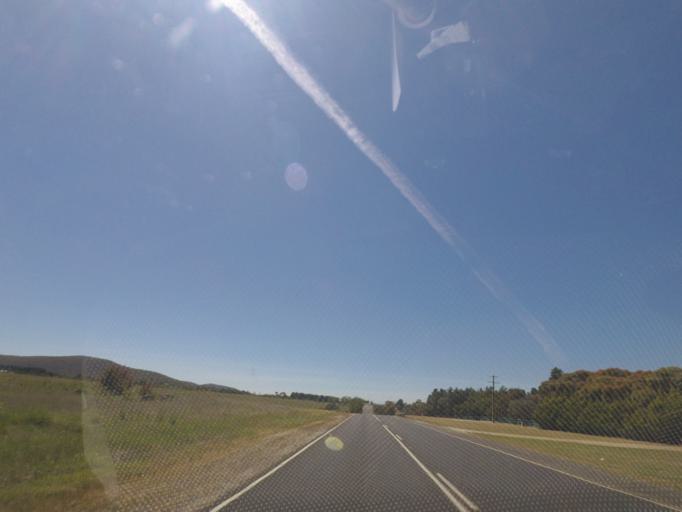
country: AU
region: Victoria
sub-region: Hume
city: Sunbury
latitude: -37.4727
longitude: 144.6445
